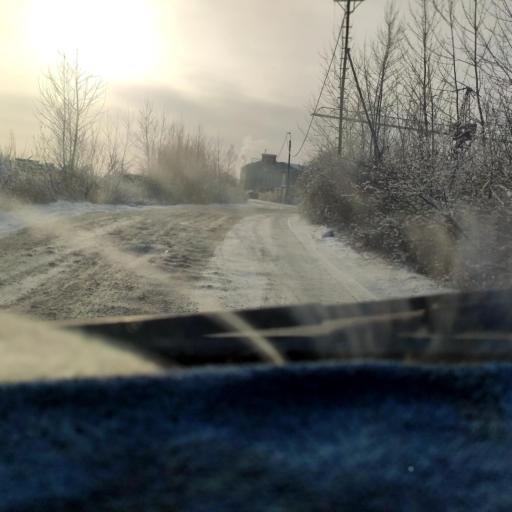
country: RU
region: Bashkortostan
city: Avdon
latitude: 54.6714
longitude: 55.8154
